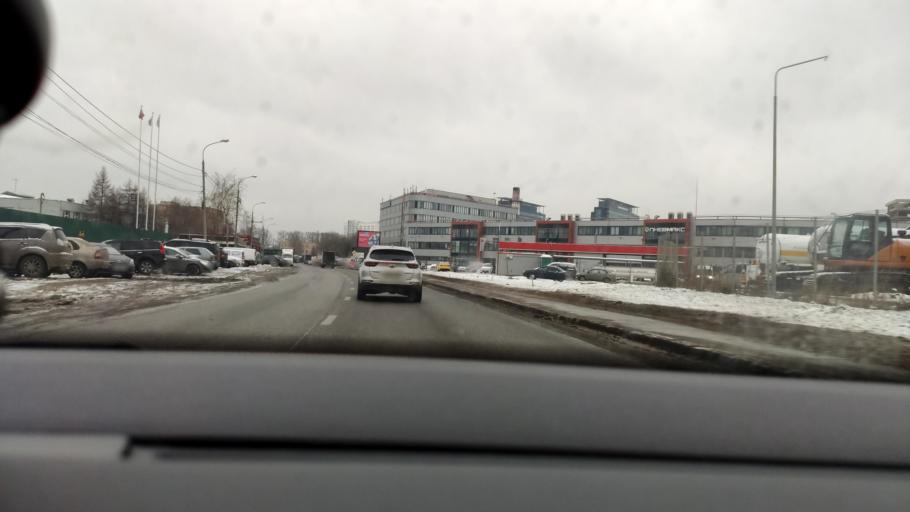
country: RU
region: Moscow
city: Khimki
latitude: 55.9135
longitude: 37.4200
